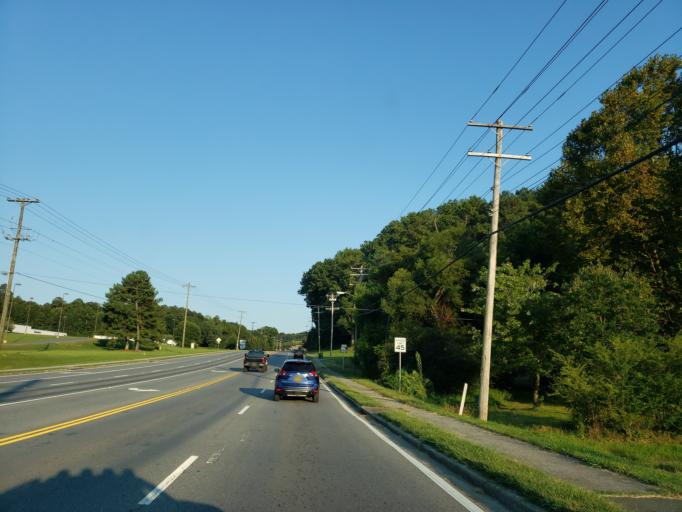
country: US
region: Georgia
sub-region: Gordon County
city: Calhoun
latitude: 34.5140
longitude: -84.9448
